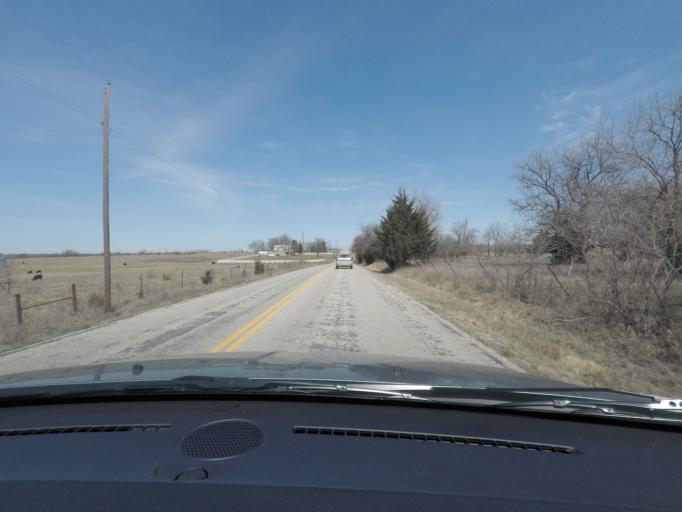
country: US
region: Kansas
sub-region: Lyon County
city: Emporia
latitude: 38.6126
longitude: -96.1697
